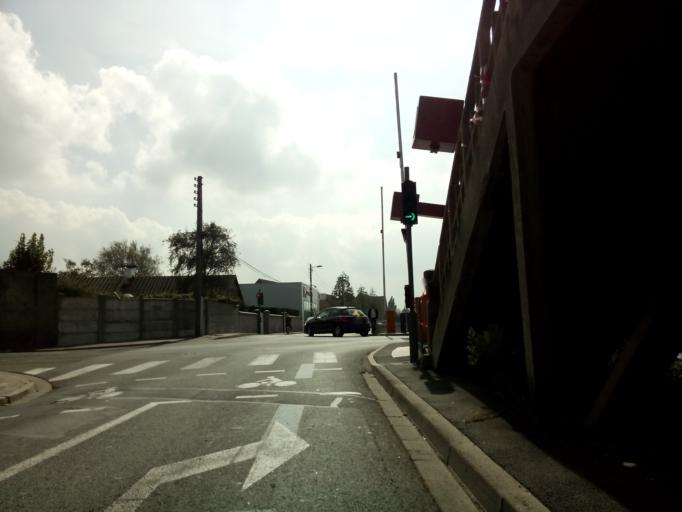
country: FR
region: Nord-Pas-de-Calais
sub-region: Departement du Pas-de-Calais
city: Calais
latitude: 50.9403
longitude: 1.8705
